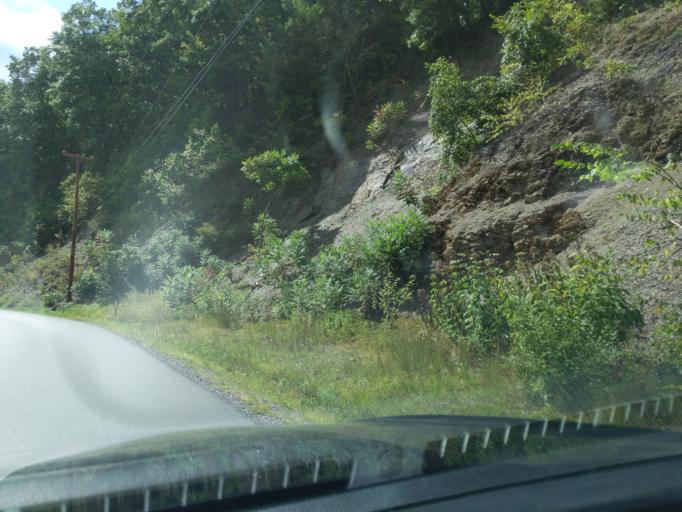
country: US
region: Pennsylvania
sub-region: Blair County
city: Tyrone
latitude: 40.7024
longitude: -78.2209
